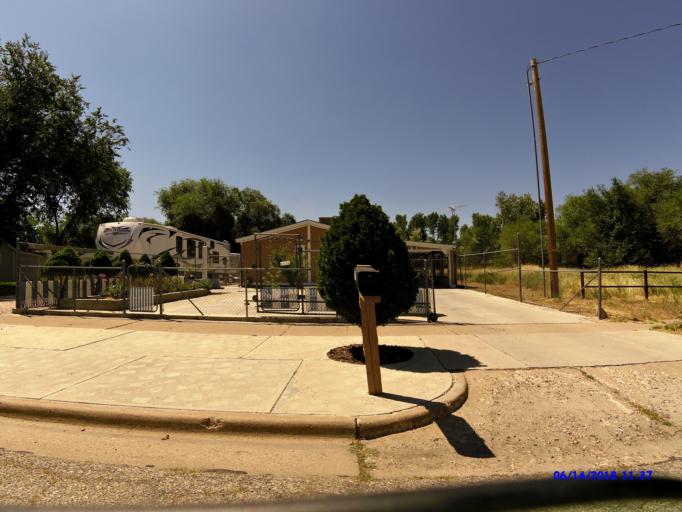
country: US
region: Utah
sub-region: Weber County
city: Ogden
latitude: 41.2209
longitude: -111.9952
